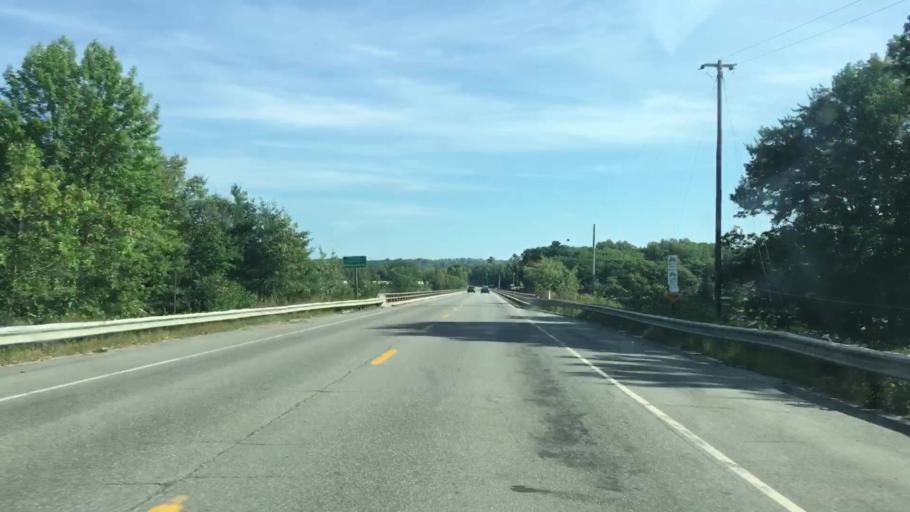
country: US
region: Maine
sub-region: Penobscot County
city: Lincoln
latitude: 45.3641
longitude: -68.5495
